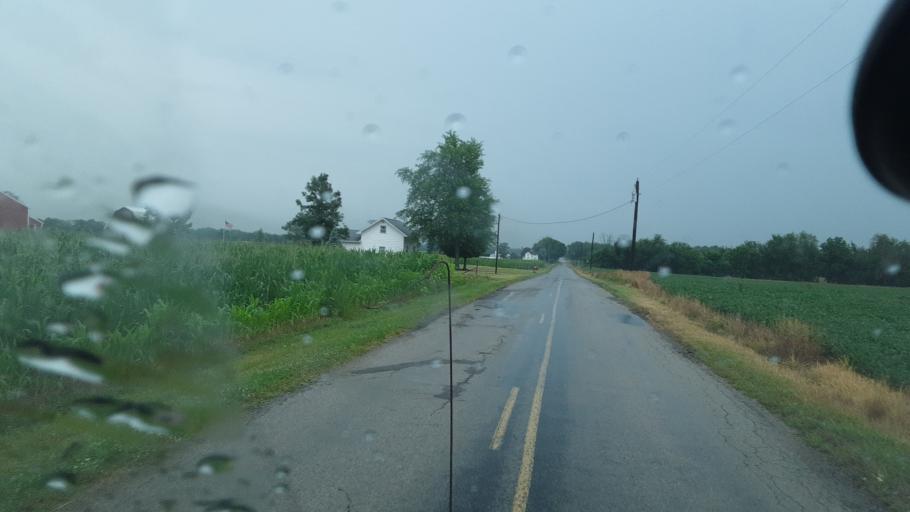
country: US
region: Ohio
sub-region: Williams County
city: Edgerton
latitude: 41.4942
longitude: -84.8148
